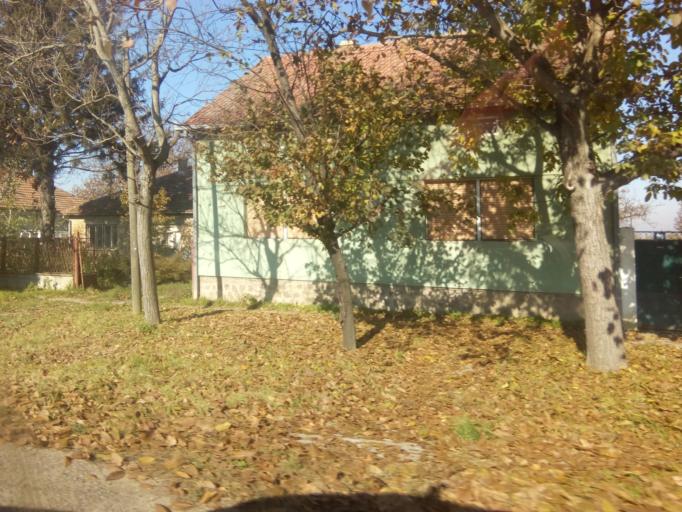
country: RS
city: Glozan
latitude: 45.2417
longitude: 19.6198
